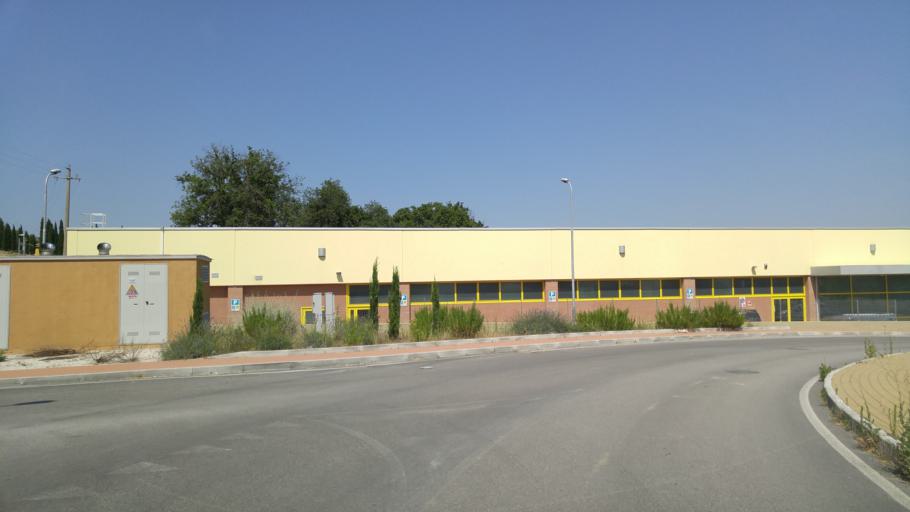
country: IT
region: The Marches
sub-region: Provincia di Pesaro e Urbino
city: Fossombrone
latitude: 43.7030
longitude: 12.8316
